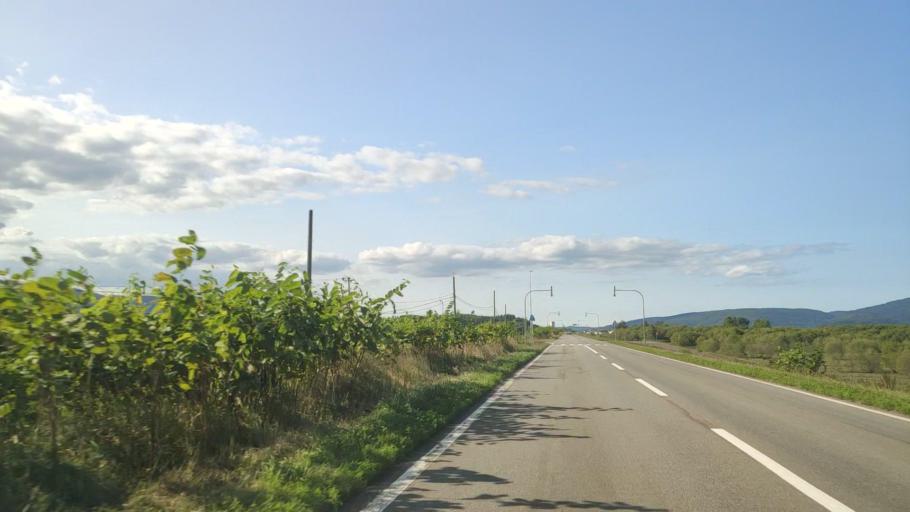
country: JP
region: Hokkaido
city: Nayoro
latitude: 44.8066
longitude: 142.0670
